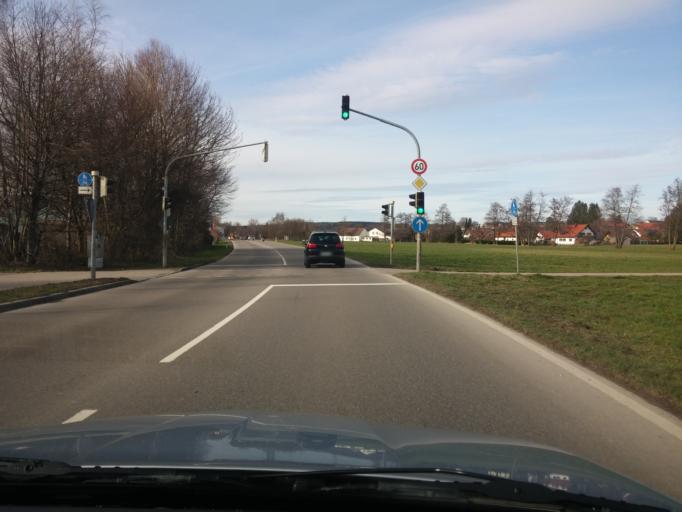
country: DE
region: Bavaria
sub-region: Swabia
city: Memmingen
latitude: 47.9855
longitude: 10.2028
